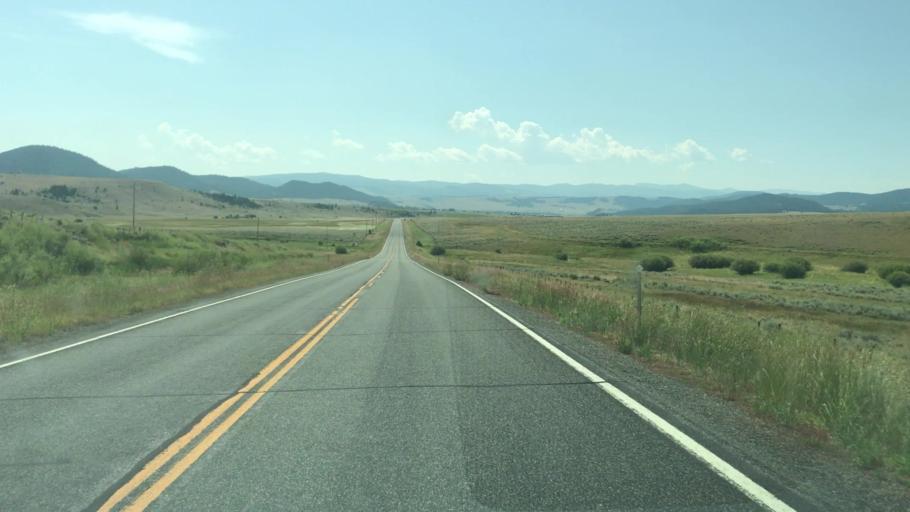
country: US
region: Montana
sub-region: Powell County
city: Deer Lodge
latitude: 46.6505
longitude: -112.6398
